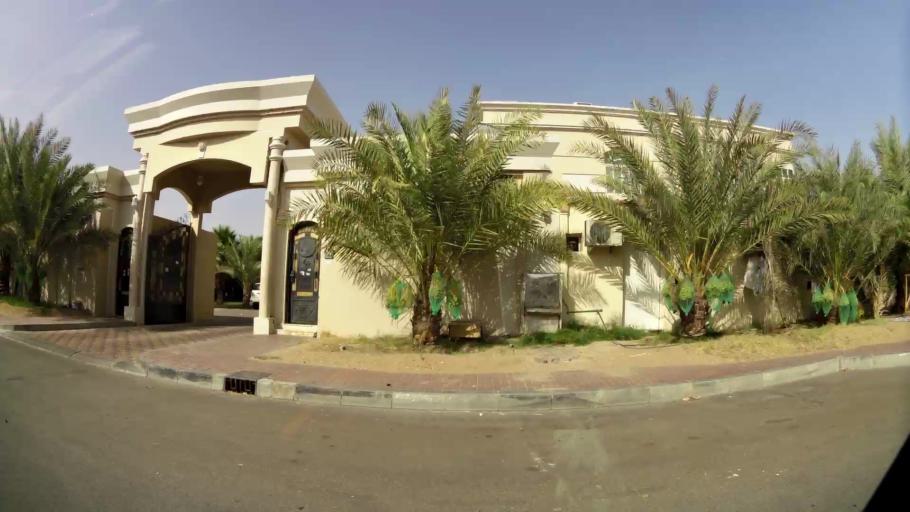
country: AE
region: Abu Dhabi
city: Al Ain
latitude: 24.2326
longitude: 55.6643
